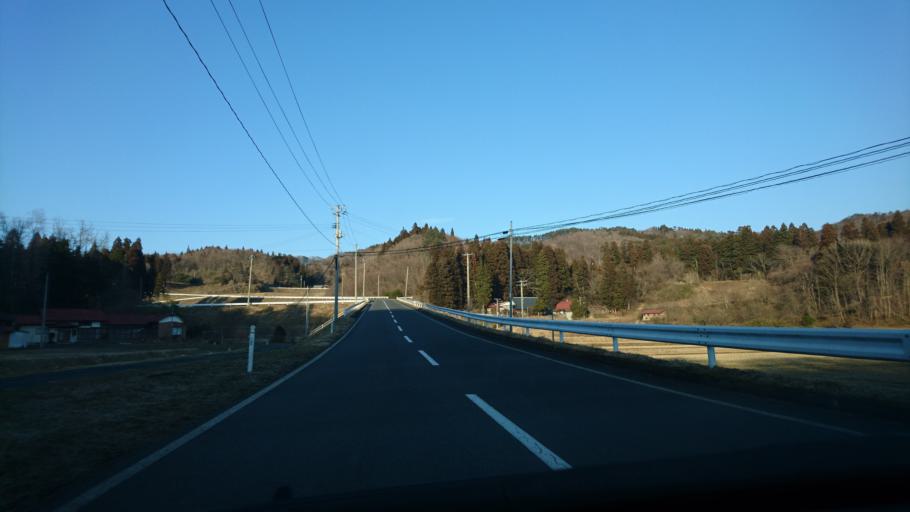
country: JP
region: Iwate
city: Ichinoseki
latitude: 39.0233
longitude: 141.3736
